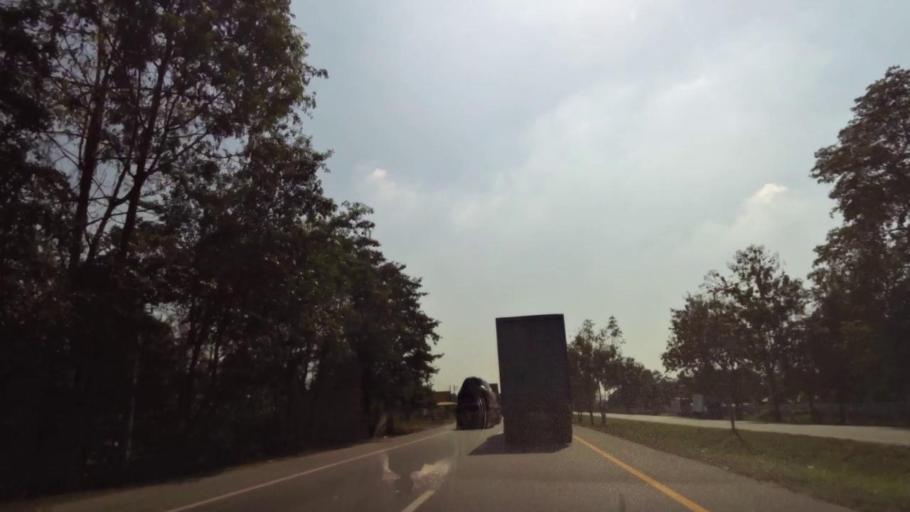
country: TH
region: Phichit
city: Bueng Na Rang
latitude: 16.1377
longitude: 100.1255
